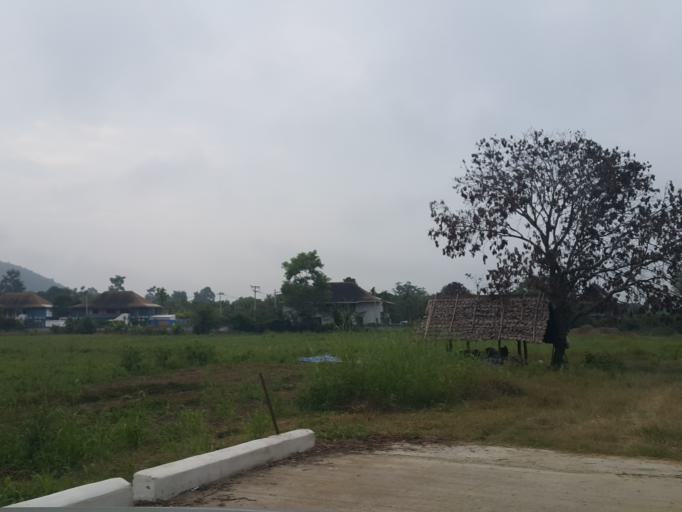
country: TH
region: Chiang Mai
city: Pai
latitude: 19.3549
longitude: 98.4451
